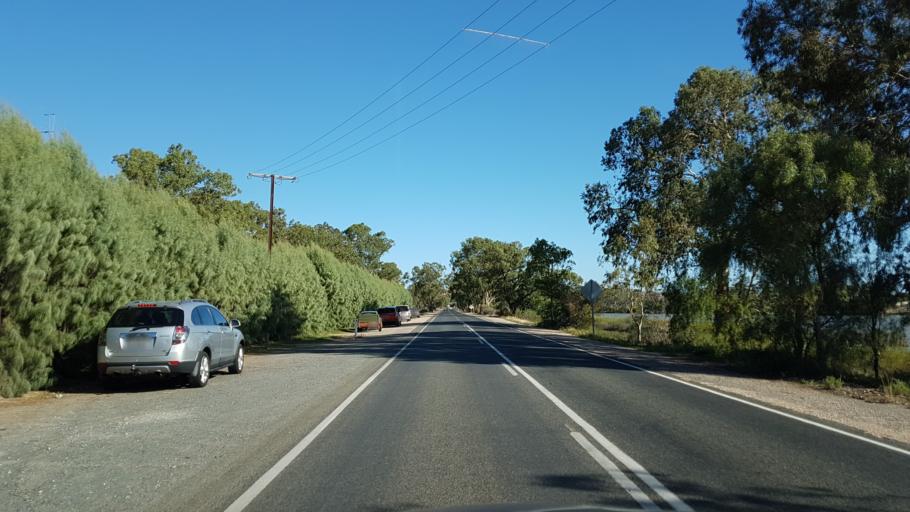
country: AU
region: South Australia
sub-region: Mid Murray
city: Mannum
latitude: -34.7571
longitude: 139.5701
